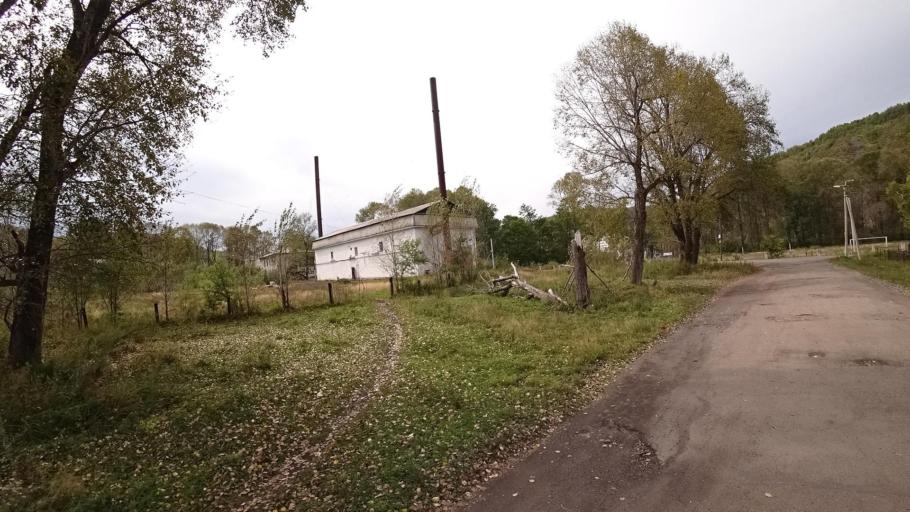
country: RU
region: Jewish Autonomous Oblast
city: Khingansk
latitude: 49.1272
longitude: 131.1963
